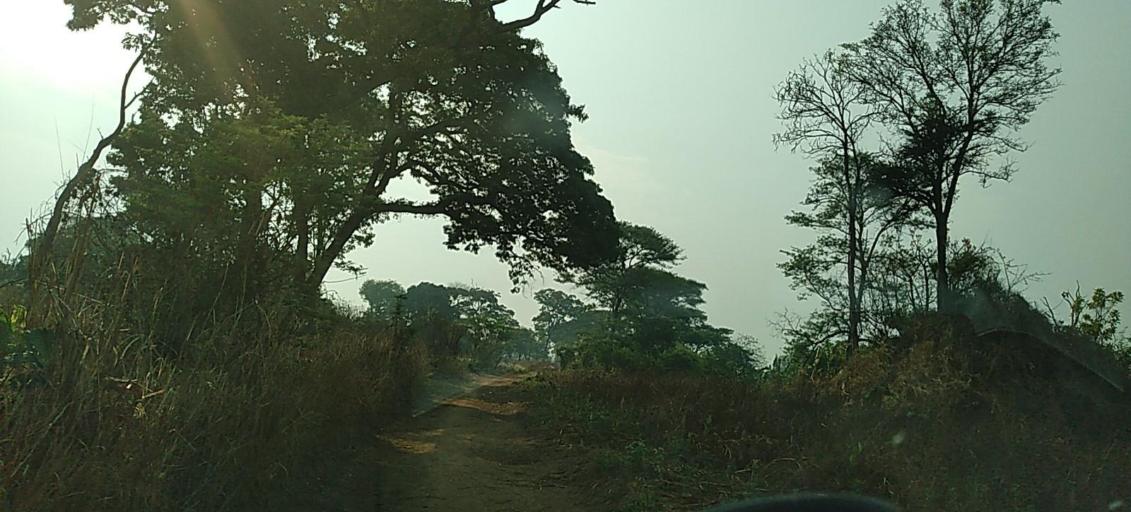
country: ZM
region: North-Western
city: Solwezi
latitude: -12.3574
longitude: 26.5490
